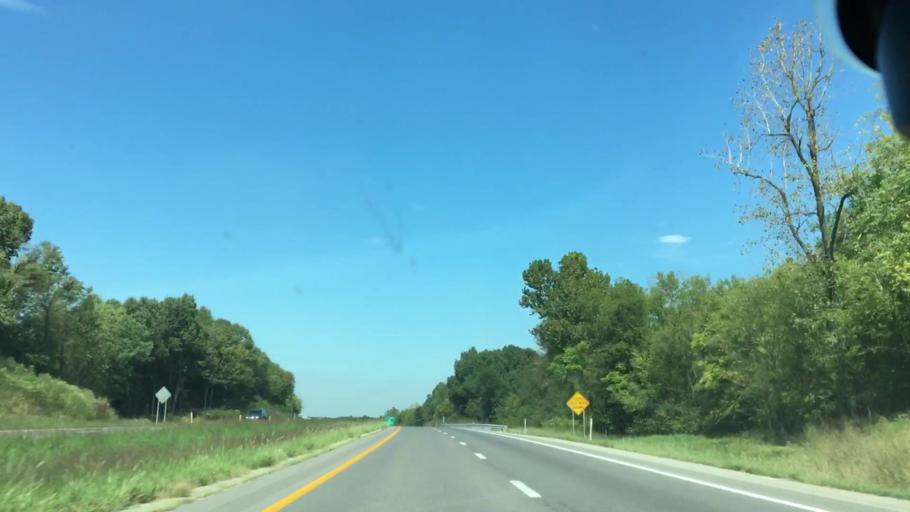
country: US
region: Kentucky
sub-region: Hopkins County
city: Earlington
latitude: 37.2807
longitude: -87.4565
